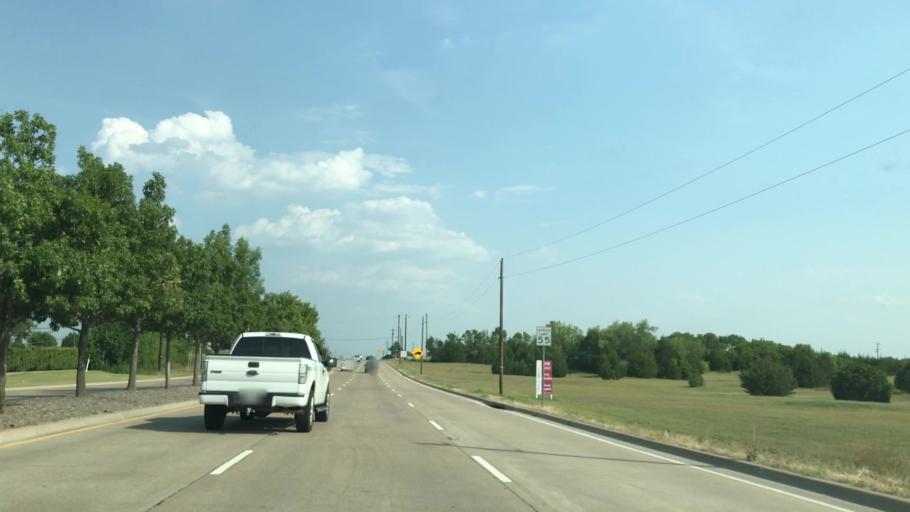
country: US
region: Texas
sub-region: Rockwall County
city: Rockwall
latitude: 32.9018
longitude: -96.4451
